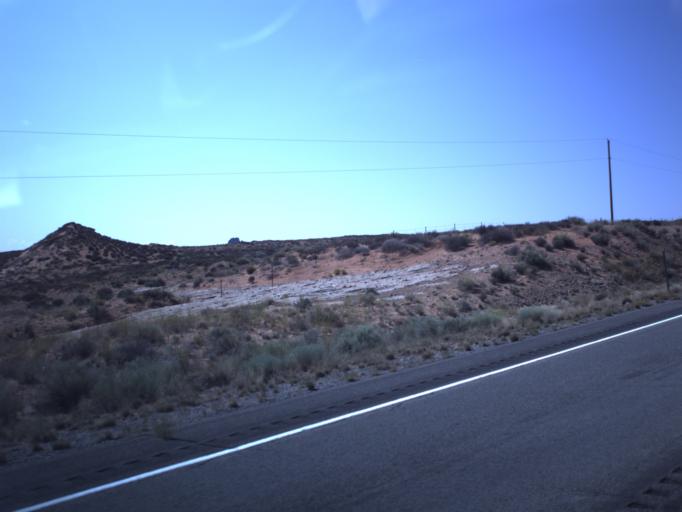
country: US
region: Utah
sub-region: San Juan County
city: Blanding
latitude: 37.0628
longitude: -109.5602
